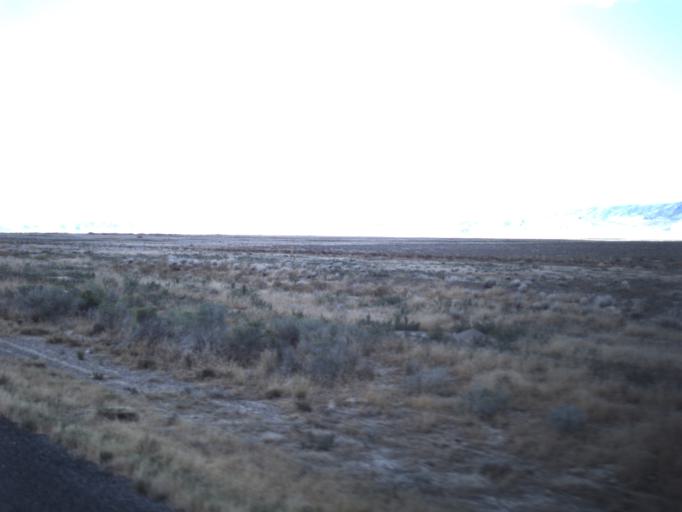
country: US
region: Utah
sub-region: Millard County
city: Delta
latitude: 38.9943
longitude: -112.7898
